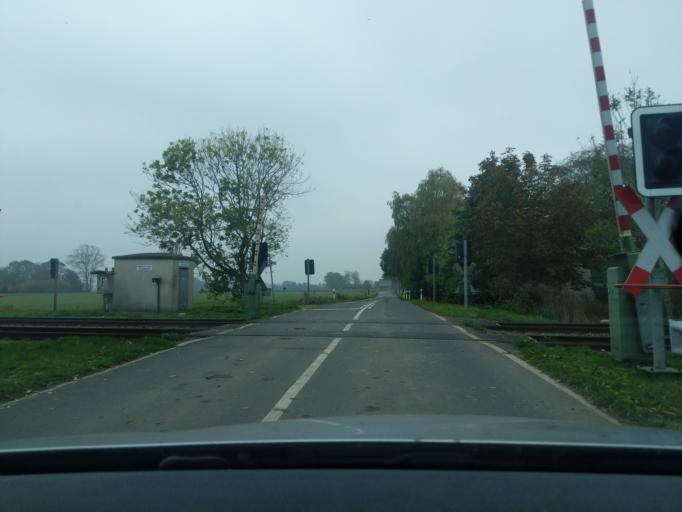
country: DE
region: Lower Saxony
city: Nordleda
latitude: 53.8255
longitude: 8.8057
